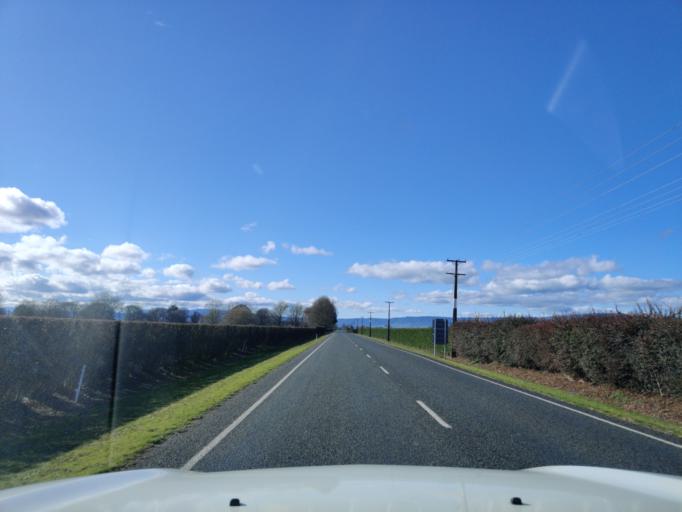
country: NZ
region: Waikato
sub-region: Matamata-Piako District
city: Matamata
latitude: -37.8776
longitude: 175.7388
